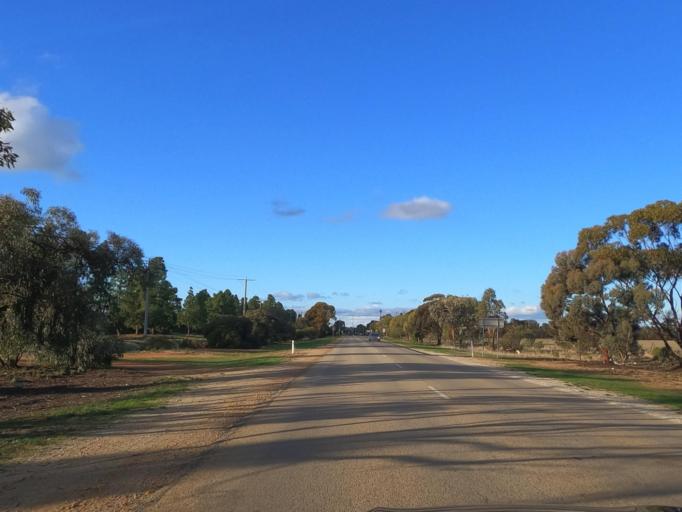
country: AU
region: Victoria
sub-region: Swan Hill
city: Swan Hill
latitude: -35.3446
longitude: 143.5268
